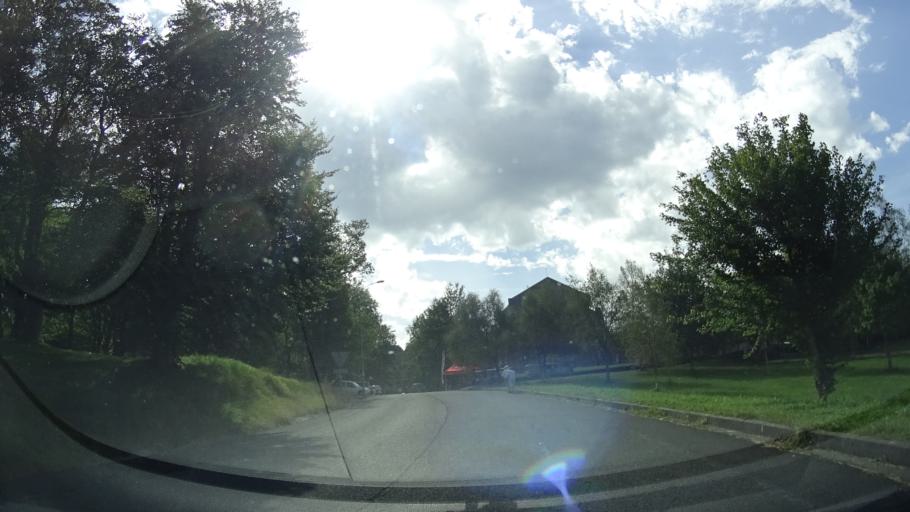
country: ES
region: Basque Country
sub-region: Bizkaia
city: Manaria
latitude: 43.1004
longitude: -2.6452
